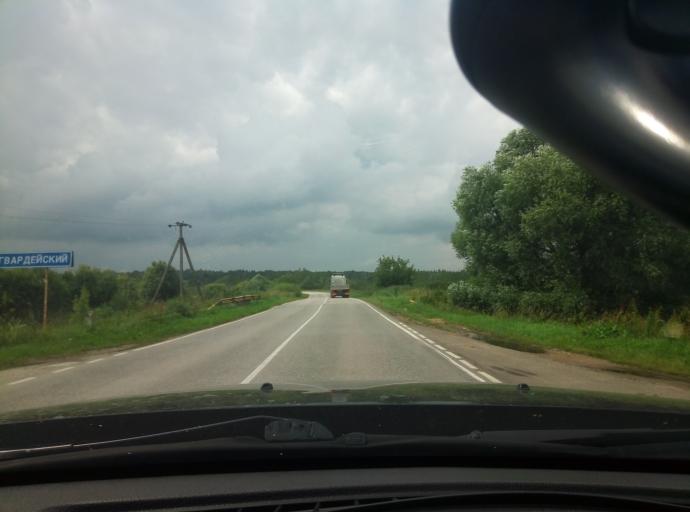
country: RU
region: Tula
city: Priupskiy
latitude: 53.9755
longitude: 37.7491
